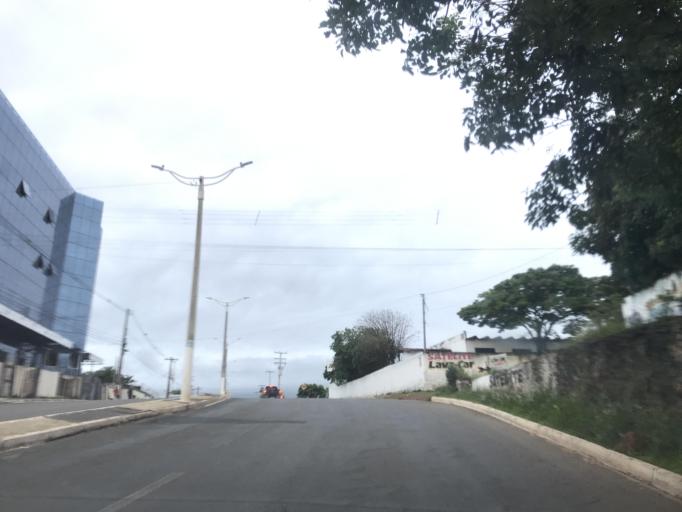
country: BR
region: Goias
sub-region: Luziania
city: Luziania
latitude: -16.2407
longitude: -47.9436
